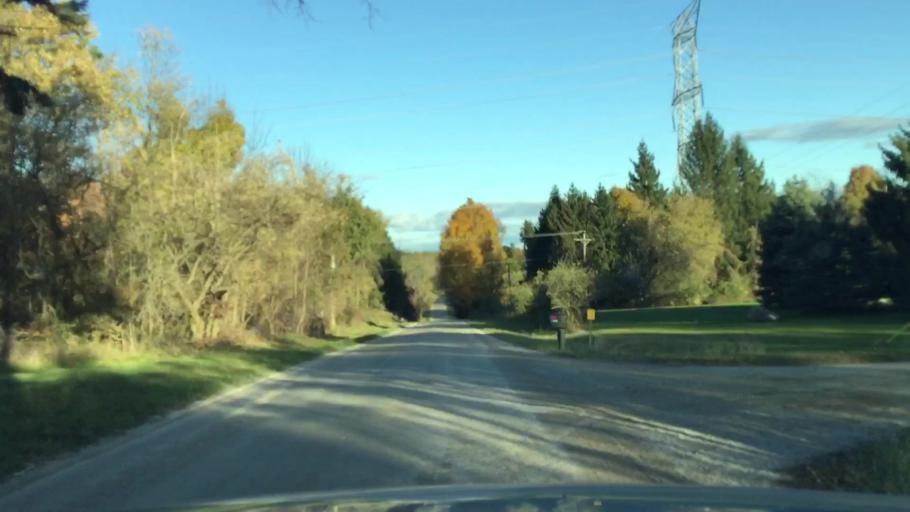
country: US
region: Michigan
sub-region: Lapeer County
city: Almont
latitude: 42.9025
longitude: -83.1327
